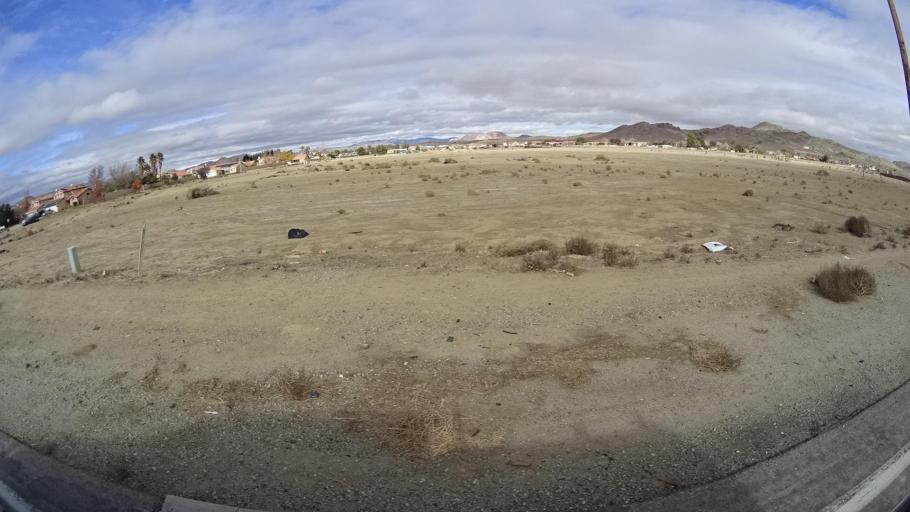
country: US
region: California
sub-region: Kern County
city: Rosamond
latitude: 34.8637
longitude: -118.2016
